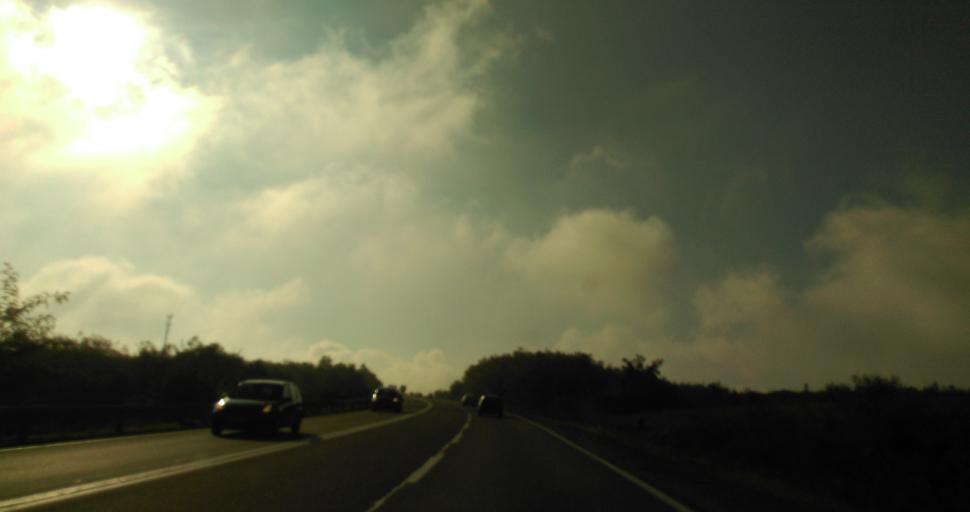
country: RS
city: Rusanj
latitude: 44.6647
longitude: 20.4263
